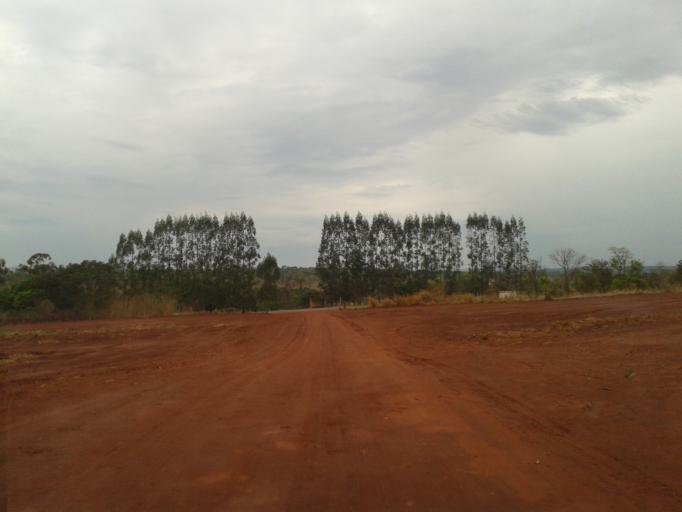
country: BR
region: Minas Gerais
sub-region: Ituiutaba
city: Ituiutaba
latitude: -18.9553
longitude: -49.7243
